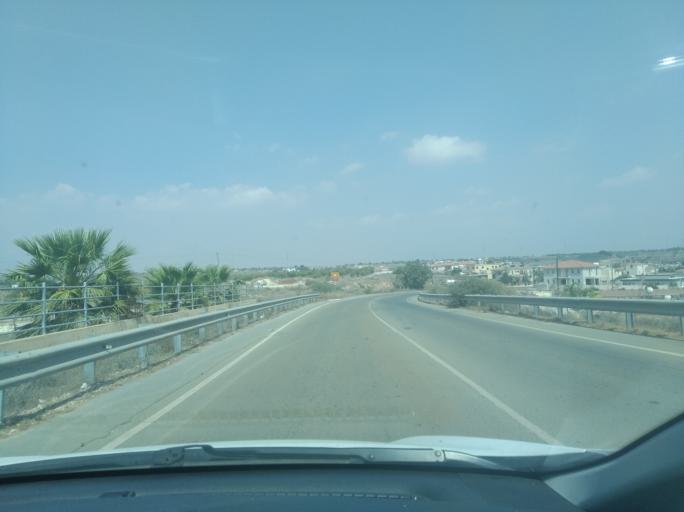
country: CY
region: Larnaka
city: Xylotymbou
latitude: 34.9925
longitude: 33.7641
